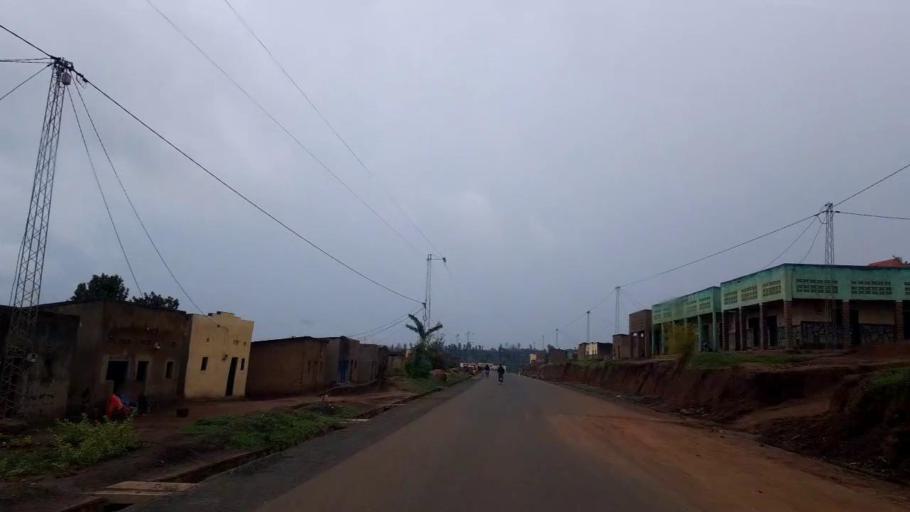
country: RW
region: Northern Province
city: Byumba
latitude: -1.4148
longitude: 30.2813
